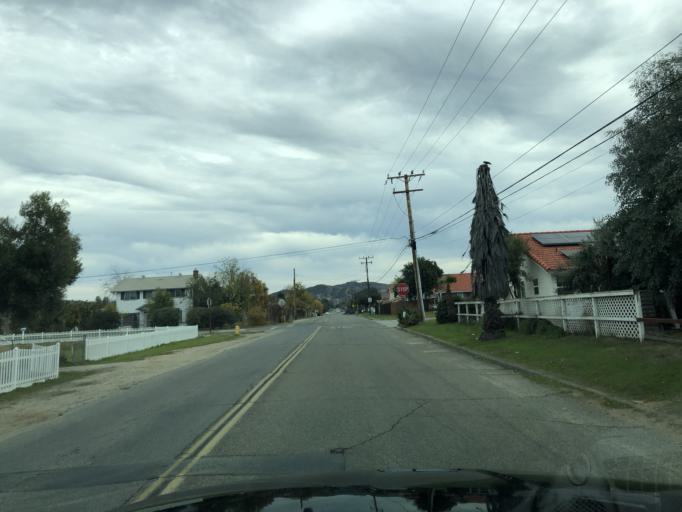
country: US
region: California
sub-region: Riverside County
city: Wildomar
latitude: 33.6196
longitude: -117.2848
